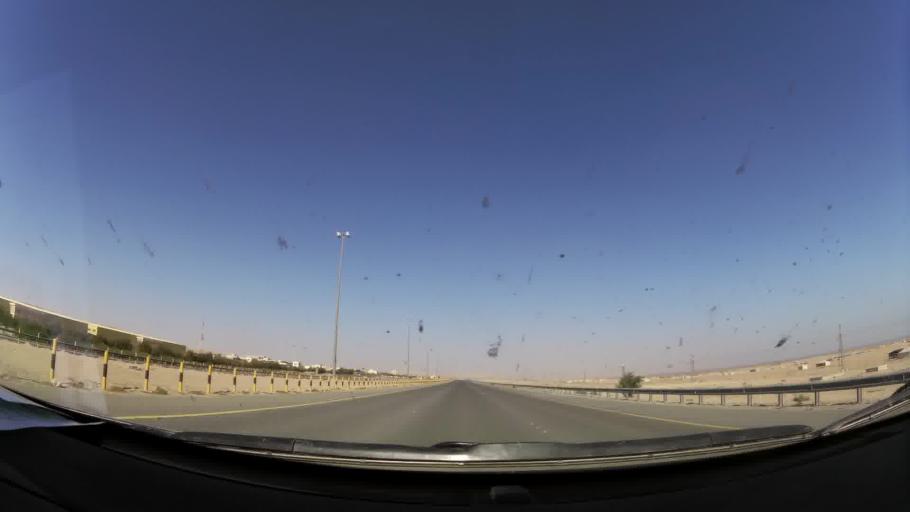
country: KW
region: Muhafazat al Jahra'
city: Al Jahra'
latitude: 29.4567
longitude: 47.7600
